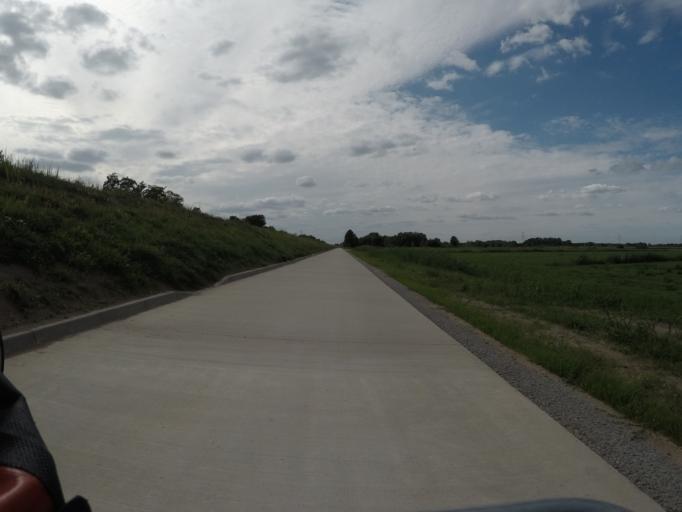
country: DE
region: Lower Saxony
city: Handorf
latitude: 53.3547
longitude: 10.3627
